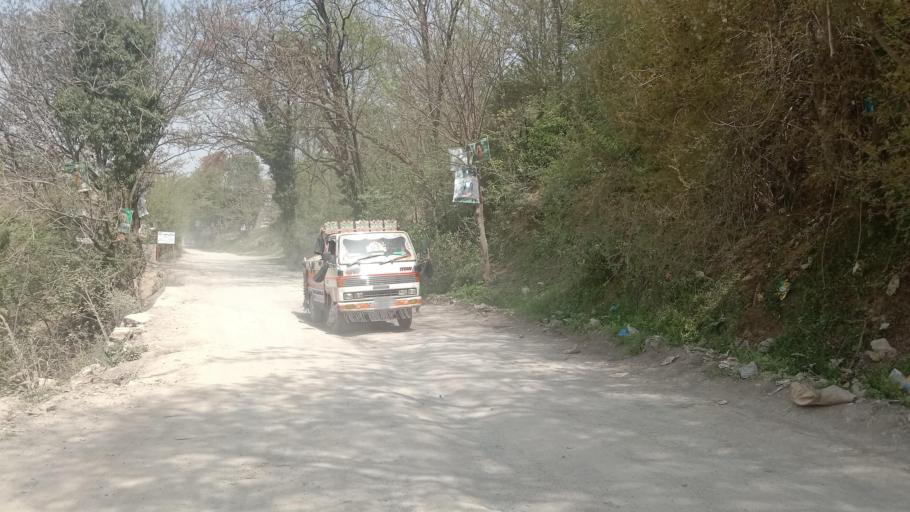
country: PK
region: Khyber Pakhtunkhwa
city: Abbottabad
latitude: 34.1589
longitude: 73.2687
